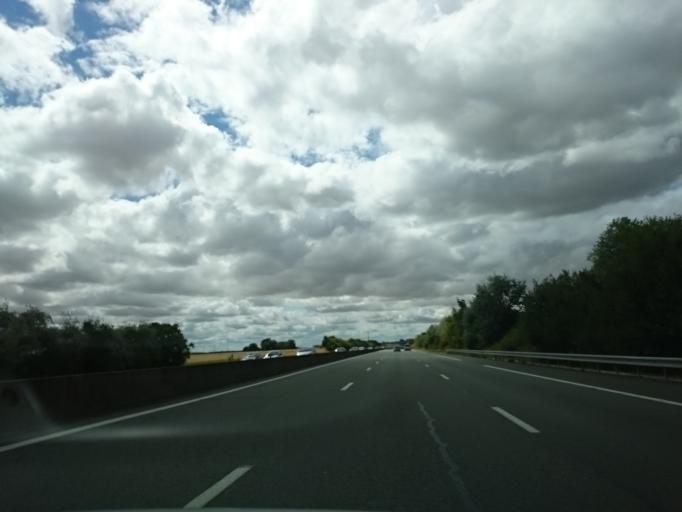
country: FR
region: Centre
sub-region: Departement d'Eure-et-Loir
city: Le Coudray
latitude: 48.4238
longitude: 1.5130
